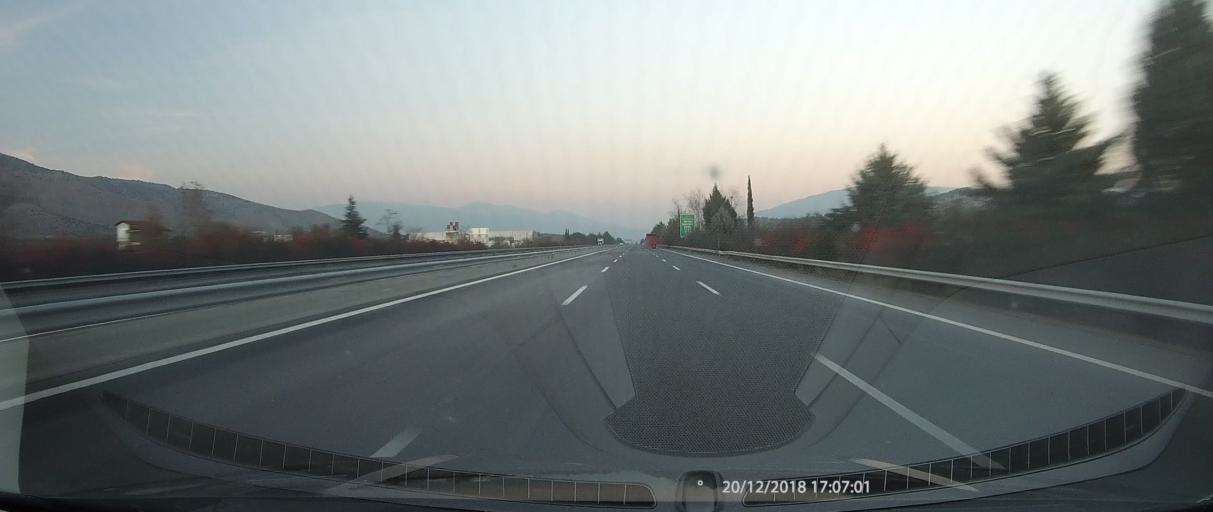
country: GR
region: Thessaly
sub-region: Nomos Larisis
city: Makrychori
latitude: 39.7696
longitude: 22.4837
